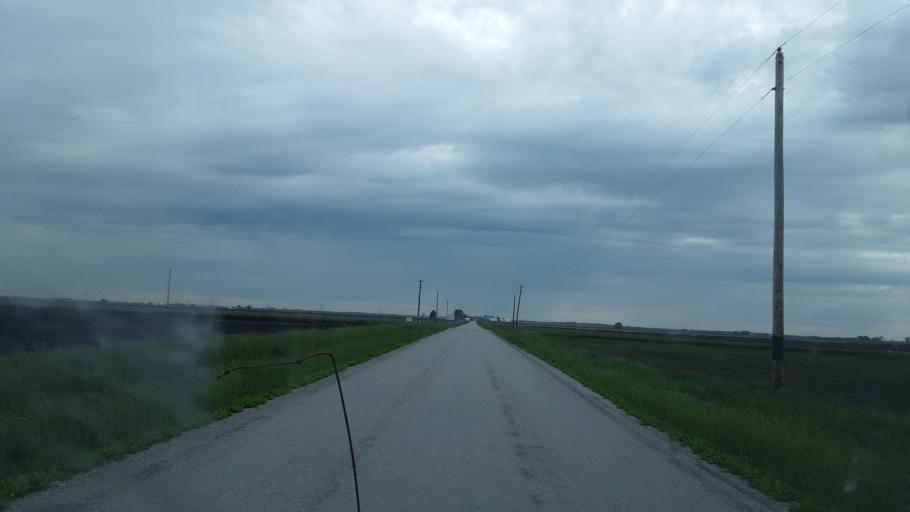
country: US
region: Illinois
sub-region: McDonough County
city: Macomb
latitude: 40.3814
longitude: -90.5462
